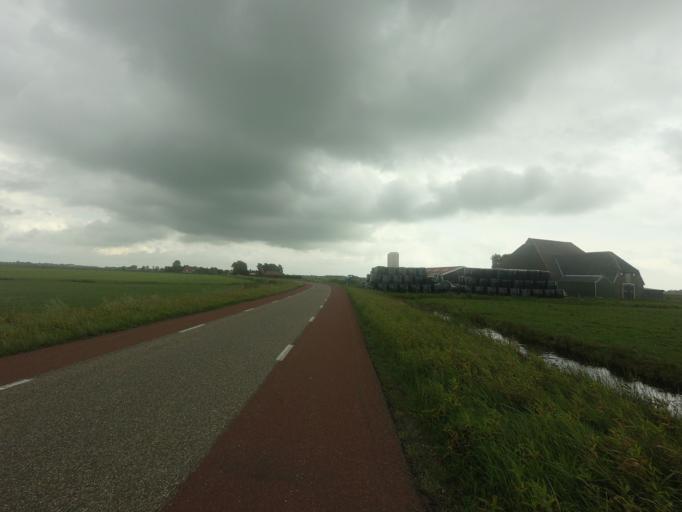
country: NL
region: Friesland
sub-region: Sudwest Fryslan
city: Workum
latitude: 53.0243
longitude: 5.4524
